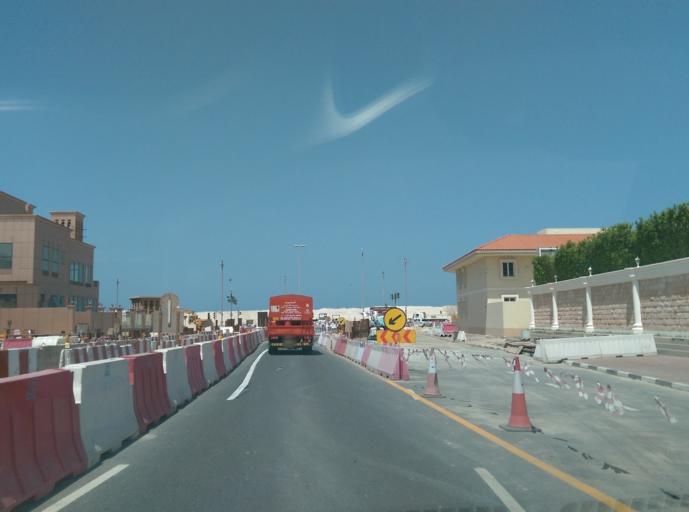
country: AE
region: Dubai
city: Dubai
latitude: 25.1927
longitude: 55.2353
